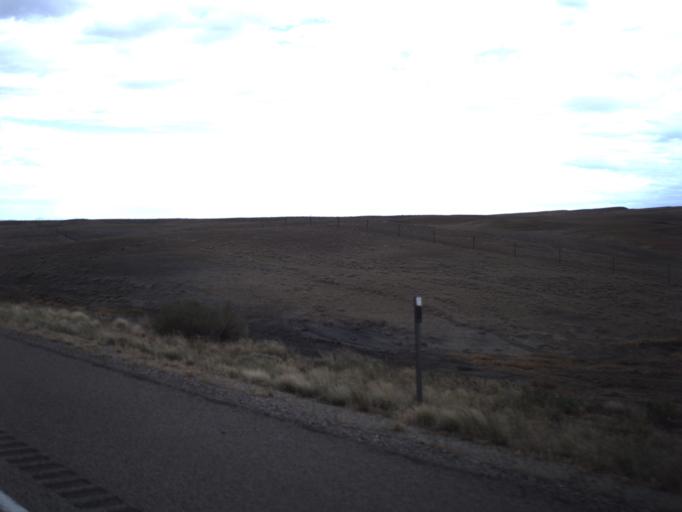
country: US
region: Utah
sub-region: Grand County
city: Moab
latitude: 38.9625
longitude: -110.0705
